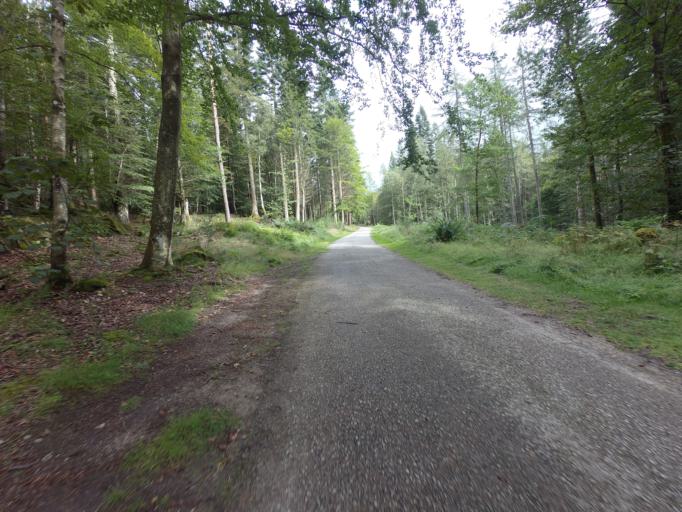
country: GB
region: Scotland
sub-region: Aberdeenshire
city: Banchory
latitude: 57.0607
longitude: -2.4510
